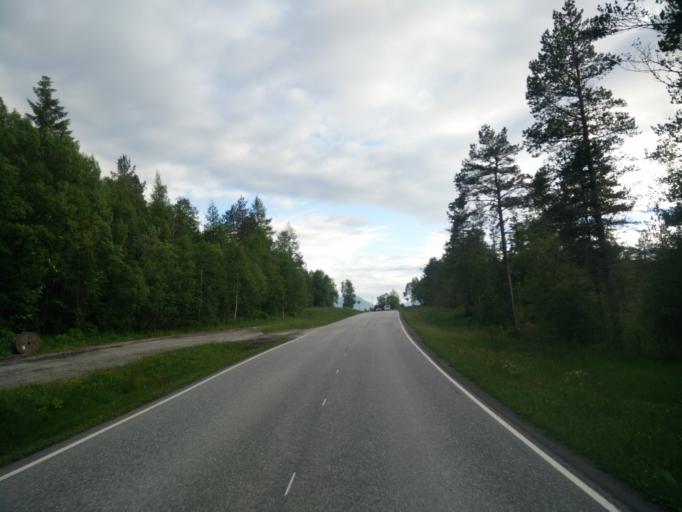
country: NO
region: More og Romsdal
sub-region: Kristiansund
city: Rensvik
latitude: 63.0249
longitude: 8.0183
